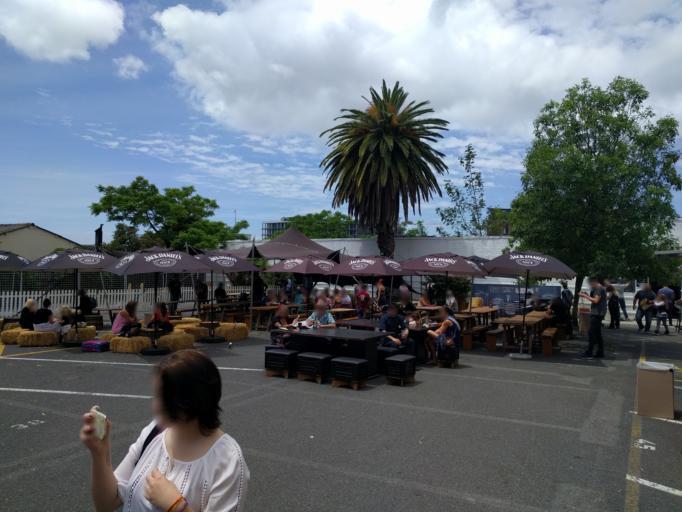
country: ZA
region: Western Cape
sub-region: City of Cape Town
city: Cape Town
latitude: -33.9325
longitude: 18.4188
